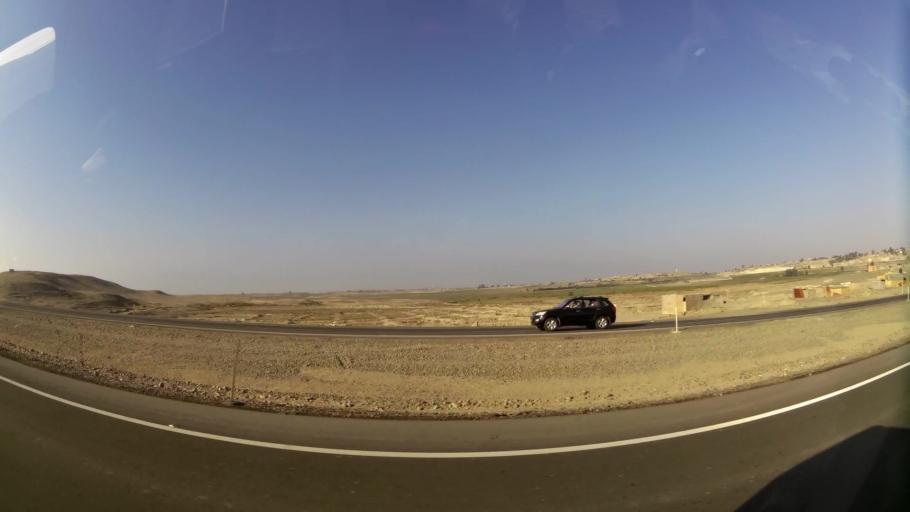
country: PE
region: Ica
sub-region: Provincia de Pisco
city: San Clemente
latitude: -13.6649
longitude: -76.1722
